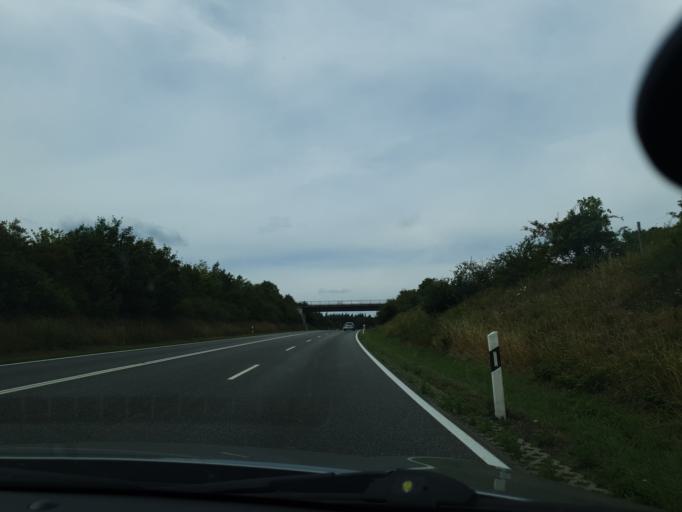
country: DE
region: Rheinland-Pfalz
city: Mayen
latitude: 50.3095
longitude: 7.2071
